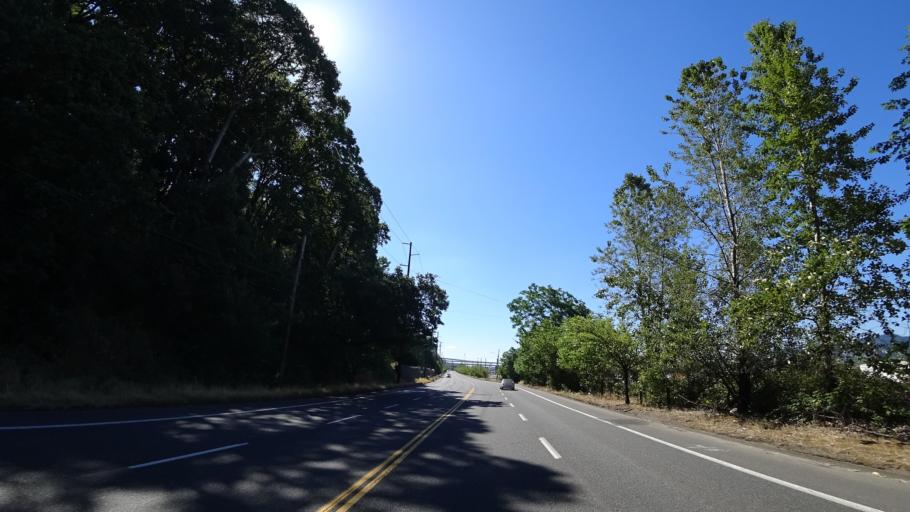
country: US
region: Oregon
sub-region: Multnomah County
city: Portland
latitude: 45.5516
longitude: -122.6896
